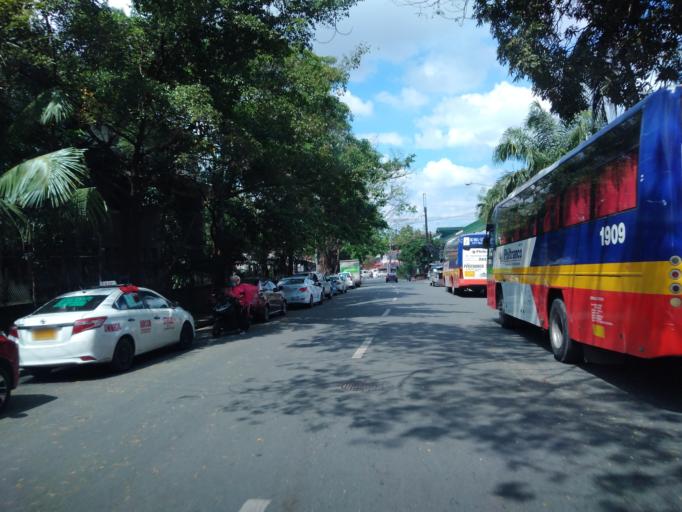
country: PH
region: Metro Manila
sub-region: Quezon City
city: Quezon City
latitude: 14.6503
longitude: 121.0536
